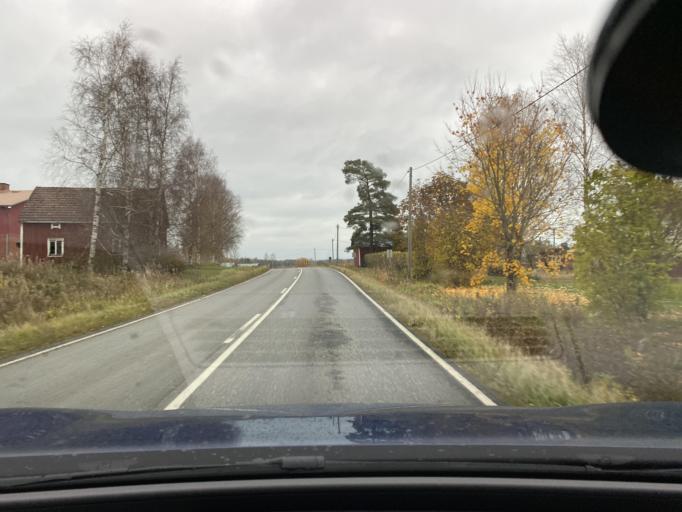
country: FI
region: Satakunta
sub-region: Pori
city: Vampula
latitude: 61.0883
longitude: 22.5434
